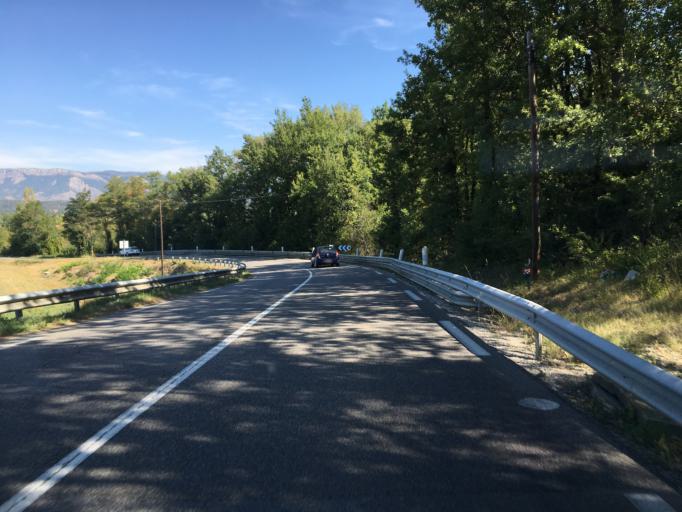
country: FR
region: Provence-Alpes-Cote d'Azur
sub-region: Departement des Hautes-Alpes
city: Laragne-Monteglin
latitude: 44.2913
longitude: 5.8431
